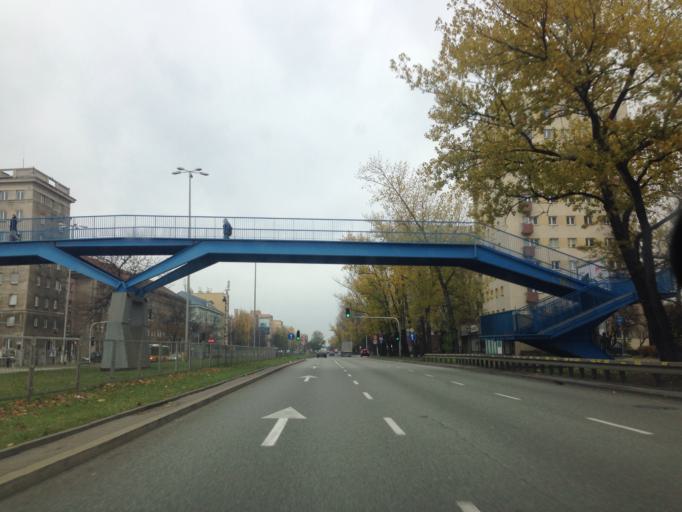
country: PL
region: Masovian Voivodeship
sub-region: Warszawa
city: Mokotow
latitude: 52.2018
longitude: 21.0501
